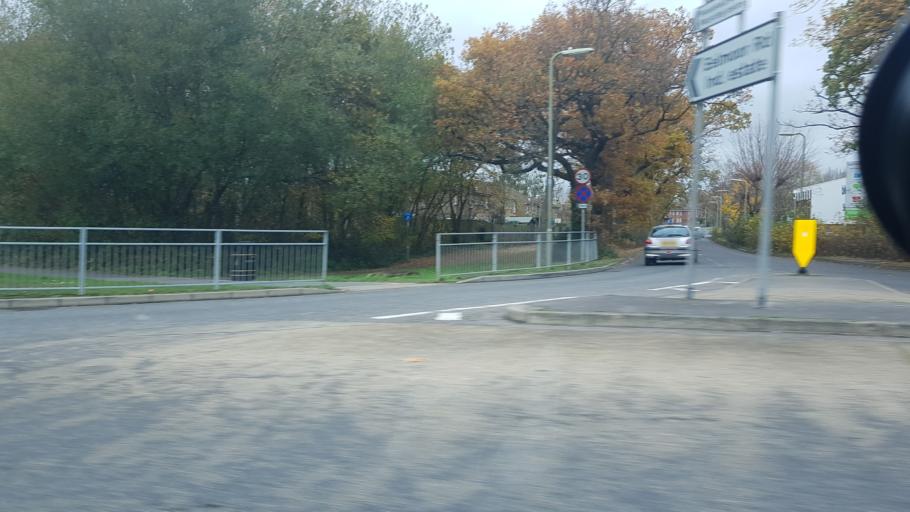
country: GB
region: England
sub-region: Hampshire
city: Farnborough
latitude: 51.2842
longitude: -0.7714
